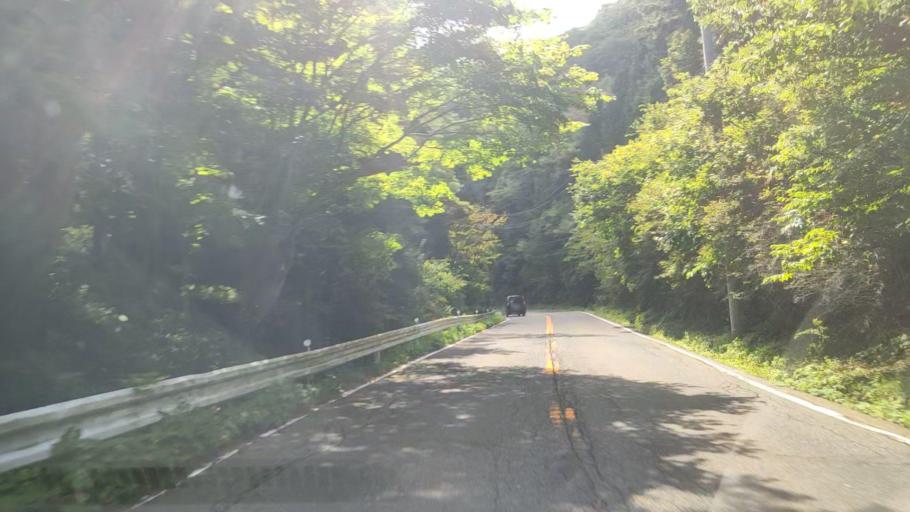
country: JP
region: Gunma
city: Shibukawa
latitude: 36.4954
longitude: 138.9062
